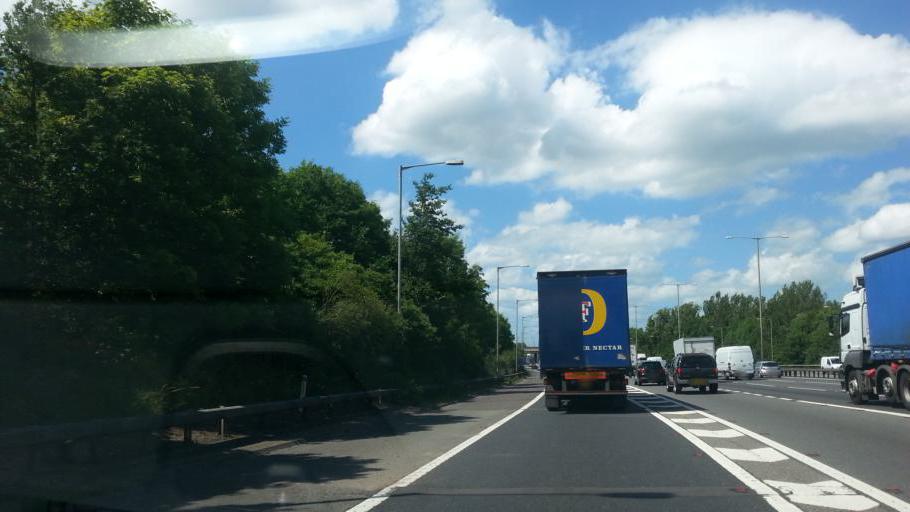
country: GB
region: England
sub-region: Buckinghamshire
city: Iver
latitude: 51.5007
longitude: -0.4962
